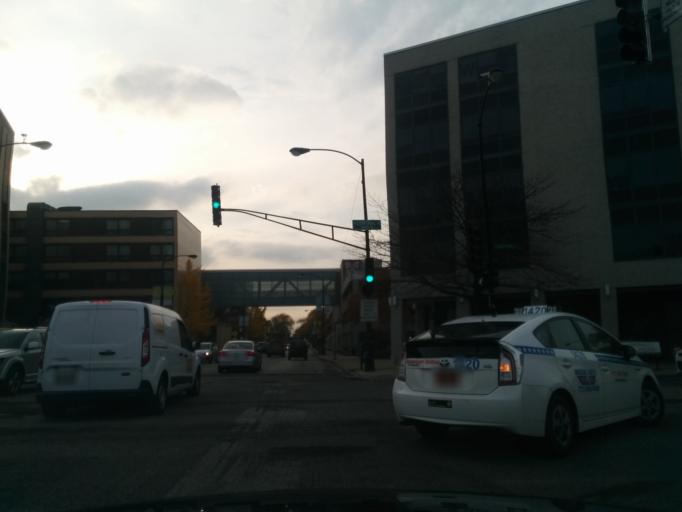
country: US
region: Illinois
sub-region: Cook County
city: Harwood Heights
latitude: 41.9458
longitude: -87.7665
